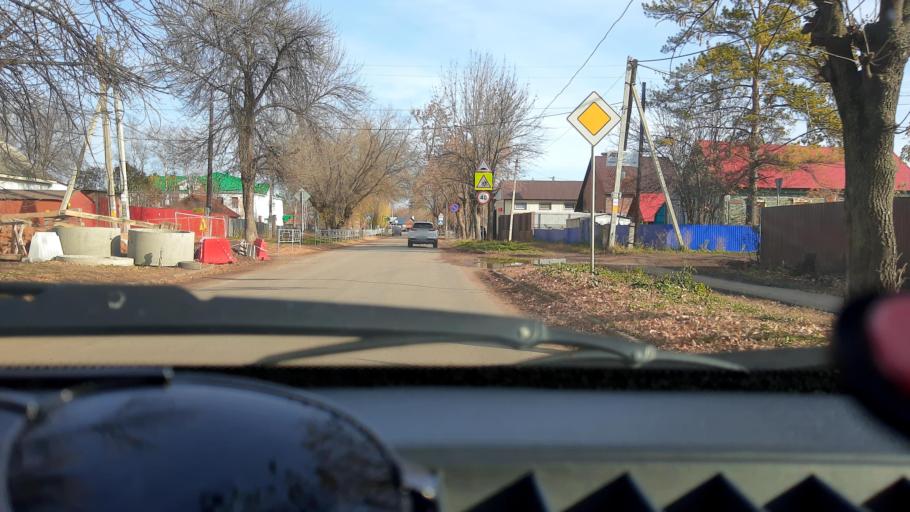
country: RU
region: Bashkortostan
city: Ufa
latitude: 54.7986
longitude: 56.1472
